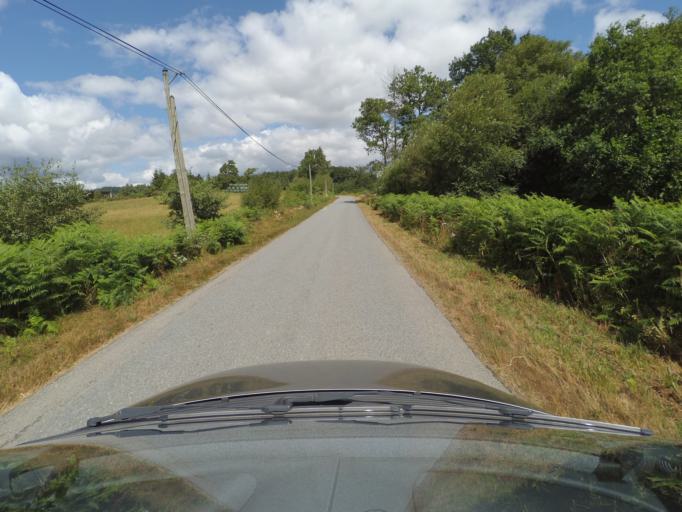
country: FR
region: Limousin
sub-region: Departement de la Creuse
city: Banize
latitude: 45.7843
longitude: 1.9366
